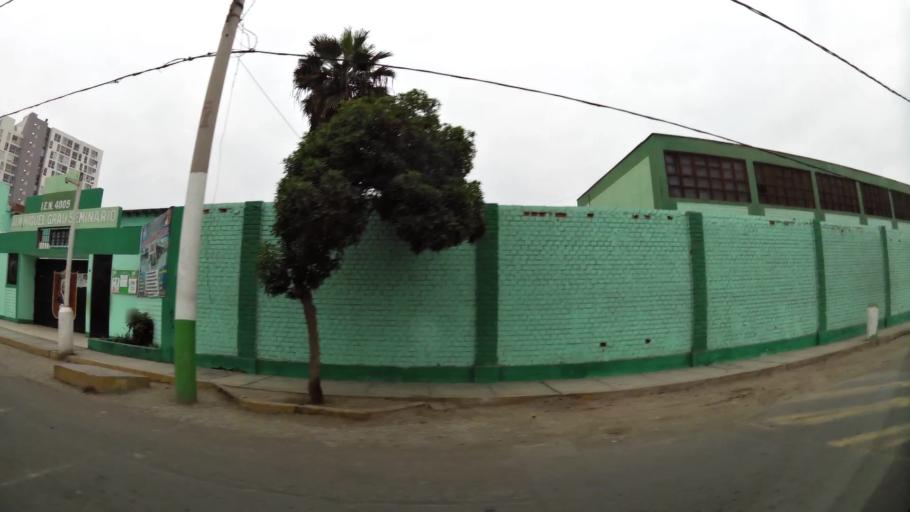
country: PE
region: Callao
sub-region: Callao
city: Callao
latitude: -12.0720
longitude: -77.1252
